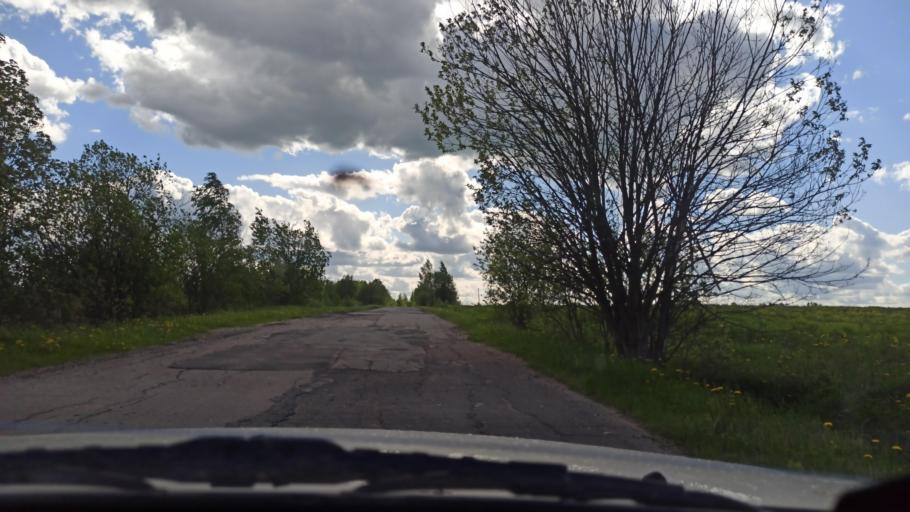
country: RU
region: Vologda
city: Molochnoye
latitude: 59.3750
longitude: 39.7094
